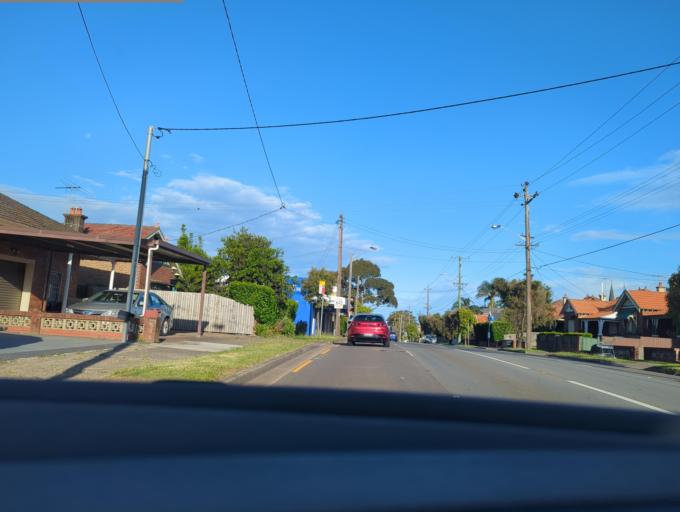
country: AU
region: New South Wales
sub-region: Rockdale
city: Bexley
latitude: -33.9496
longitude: 151.1208
